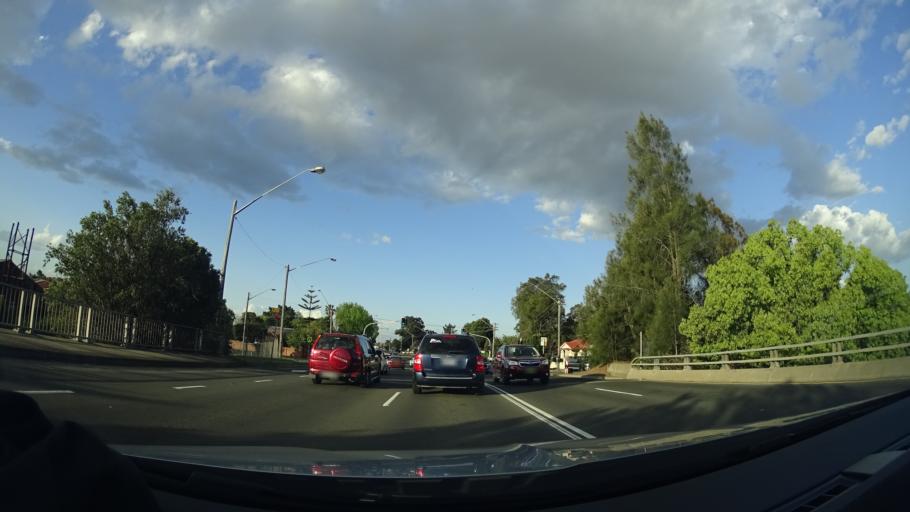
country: AU
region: New South Wales
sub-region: Canterbury
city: Belfield
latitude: -33.9067
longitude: 151.0782
